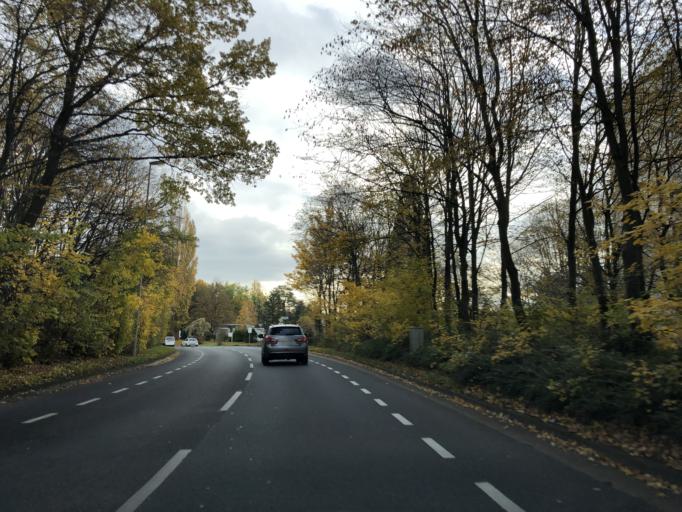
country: DE
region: North Rhine-Westphalia
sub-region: Regierungsbezirk Koln
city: Konigswinter
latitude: 50.6605
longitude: 7.1546
